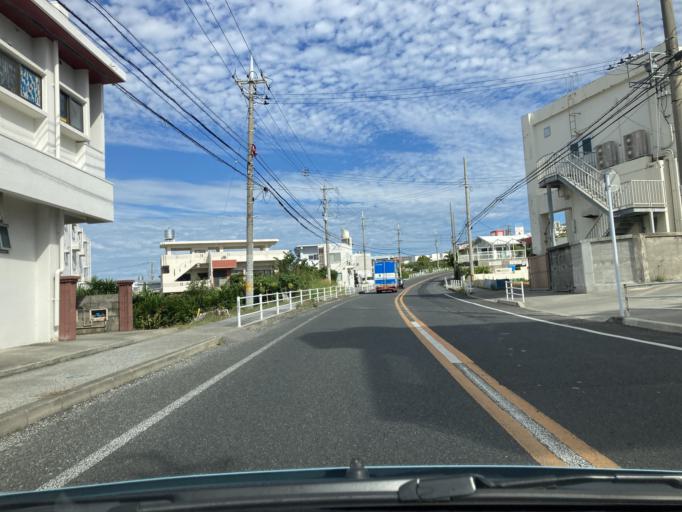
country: JP
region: Okinawa
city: Ishikawa
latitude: 26.4014
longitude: 127.7242
